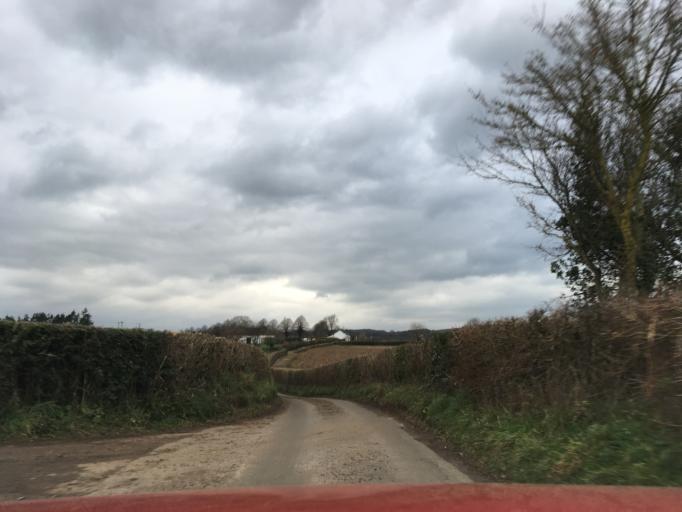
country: GB
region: Wales
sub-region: Newport
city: Llanvaches
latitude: 51.6148
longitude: -2.8130
